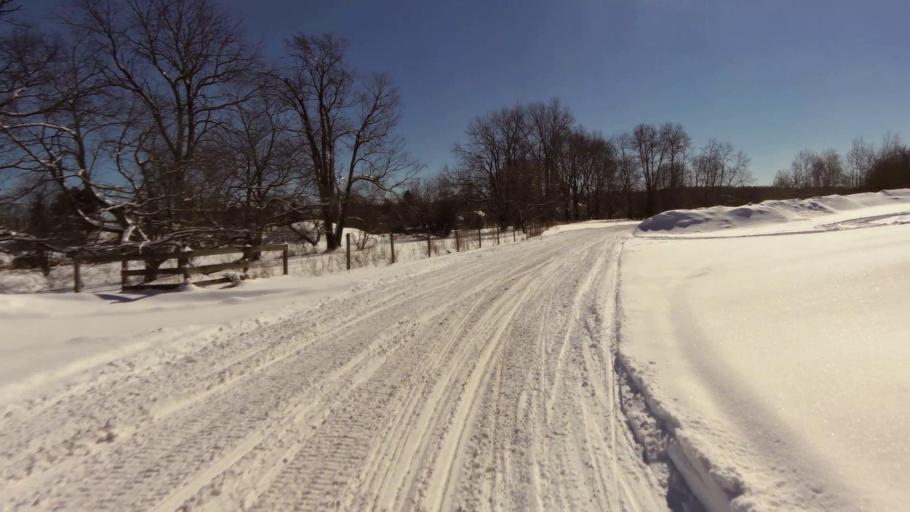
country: US
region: New York
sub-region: Chautauqua County
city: Mayville
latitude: 42.1647
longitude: -79.5838
